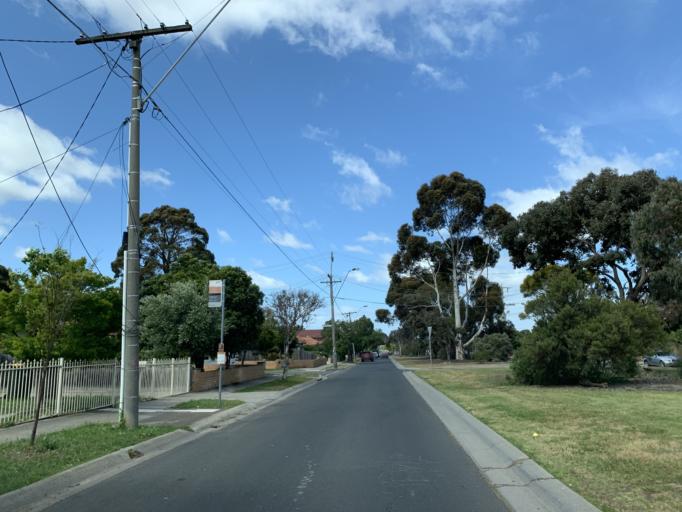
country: AU
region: Victoria
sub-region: Brimbank
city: Saint Albans
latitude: -37.7390
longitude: 144.8017
